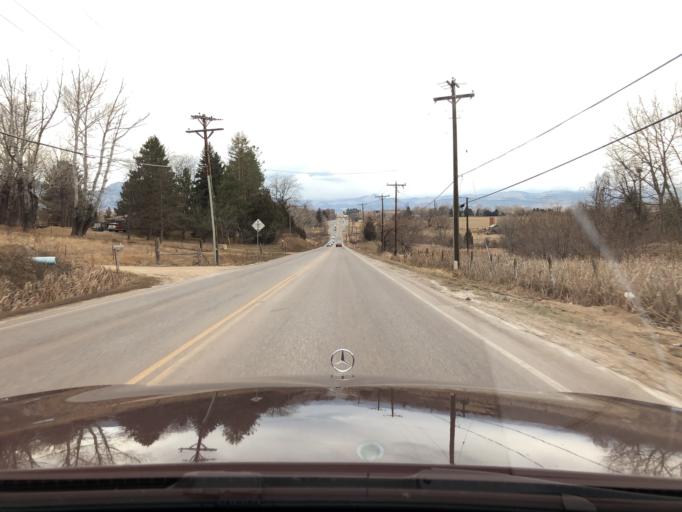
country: US
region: Colorado
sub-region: Boulder County
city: Gunbarrel
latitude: 40.0147
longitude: -105.1677
